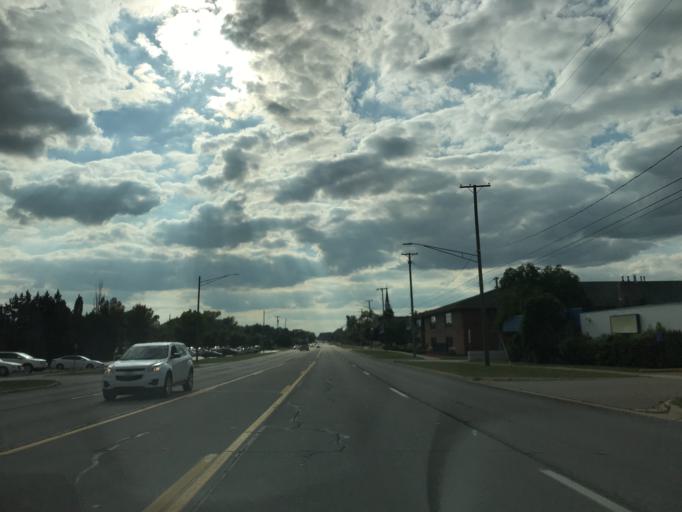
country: US
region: Michigan
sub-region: Wayne County
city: Redford
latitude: 42.4142
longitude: -83.2879
